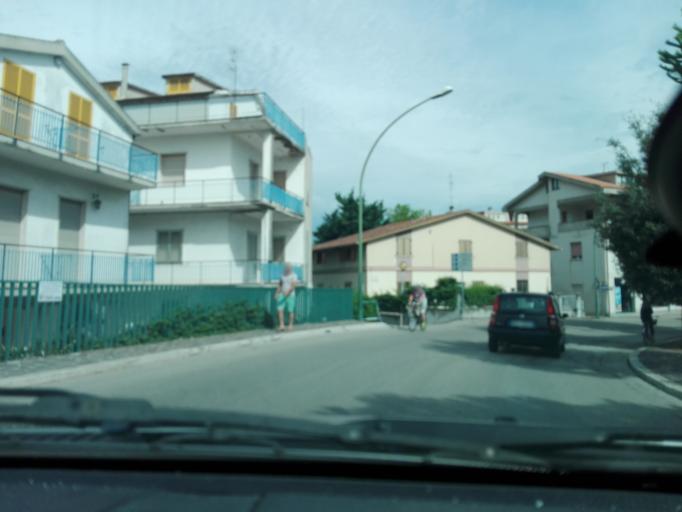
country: IT
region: Abruzzo
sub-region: Provincia di Teramo
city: Pineto
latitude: 42.6106
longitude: 14.0626
